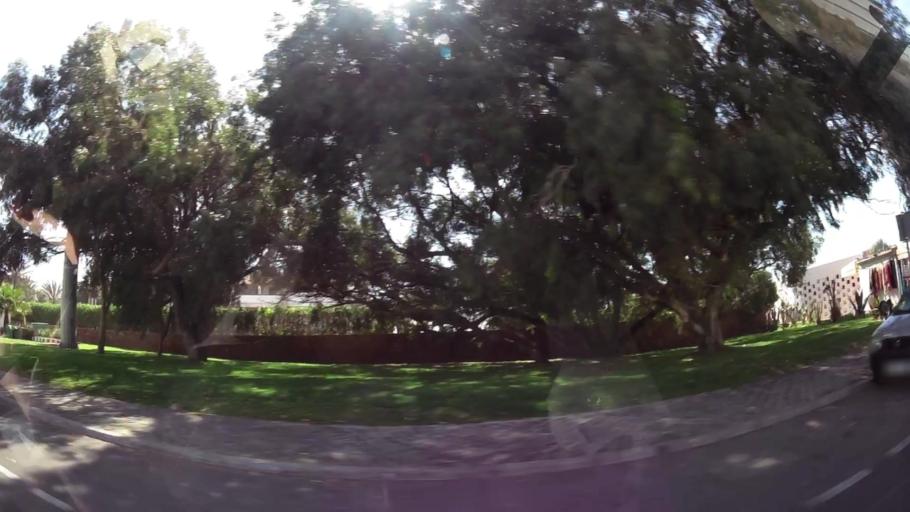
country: MA
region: Souss-Massa-Draa
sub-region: Agadir-Ida-ou-Tnan
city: Agadir
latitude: 30.4011
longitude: -9.5978
